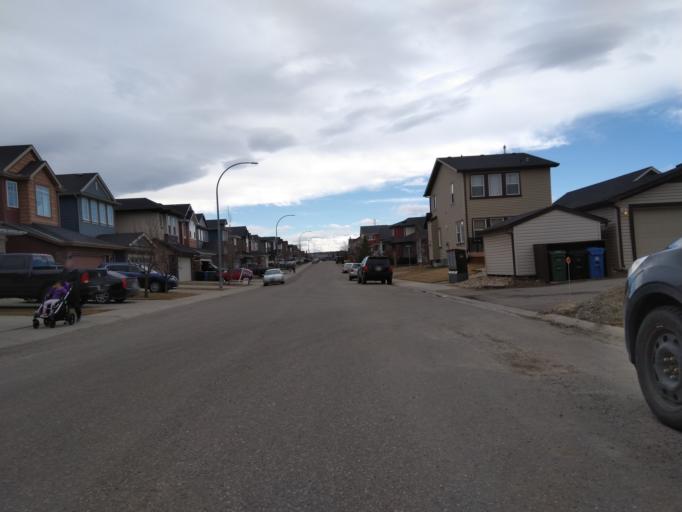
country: CA
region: Alberta
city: Calgary
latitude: 51.1715
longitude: -114.1053
